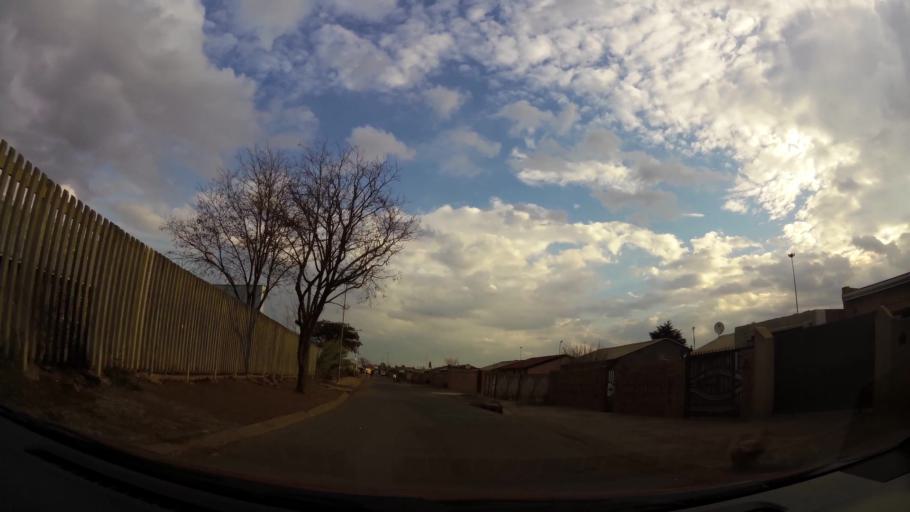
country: ZA
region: Gauteng
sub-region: City of Johannesburg Metropolitan Municipality
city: Soweto
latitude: -26.2386
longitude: 27.8225
